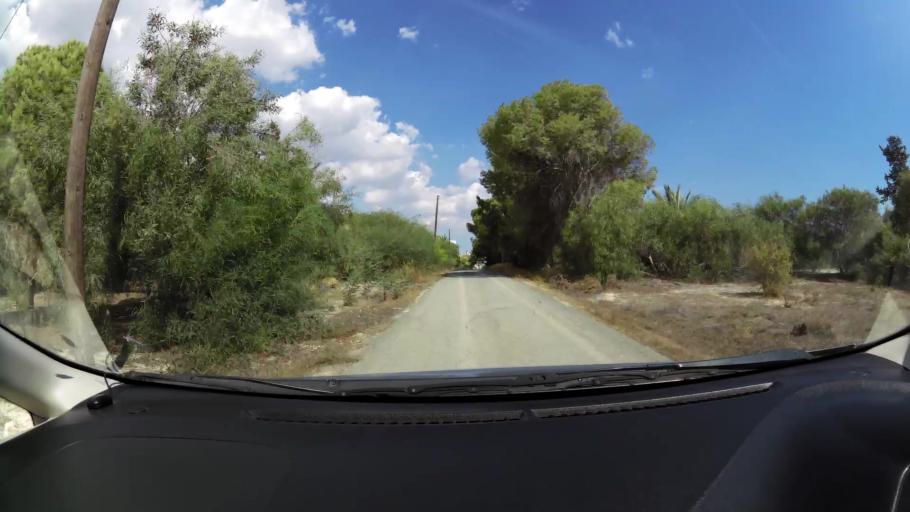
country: CY
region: Larnaka
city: Larnaca
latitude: 34.9096
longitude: 33.6160
